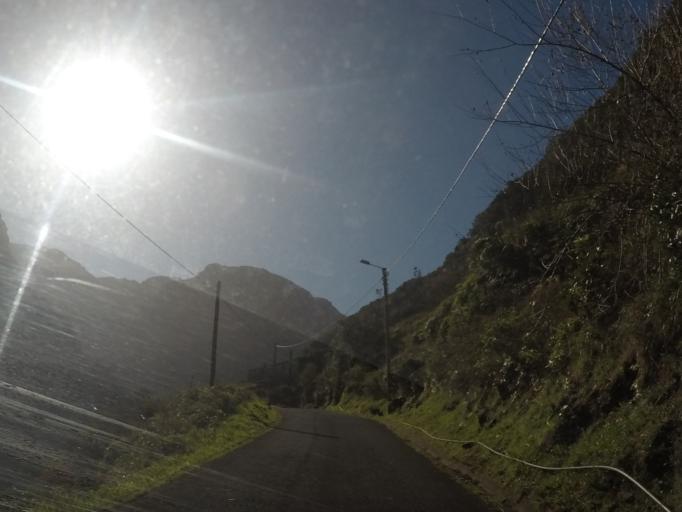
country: PT
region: Madeira
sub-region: Sao Vicente
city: Sao Vicente
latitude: 32.7924
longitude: -16.9730
